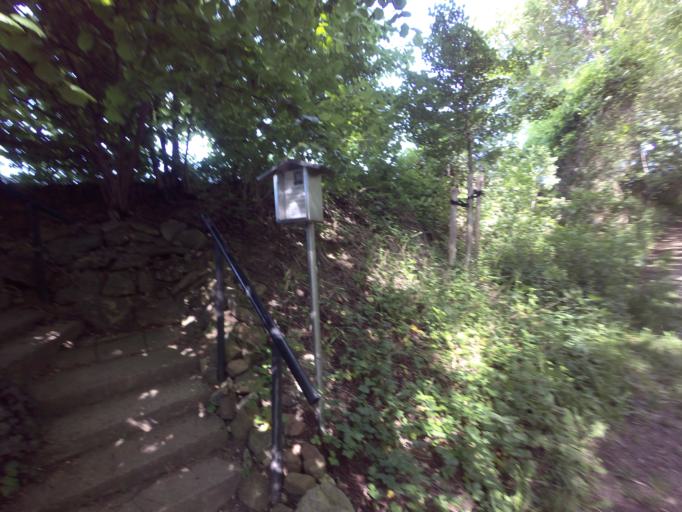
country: NL
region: Limburg
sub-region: Gemeente Voerendaal
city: Ubachsberg
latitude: 50.8129
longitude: 5.9281
